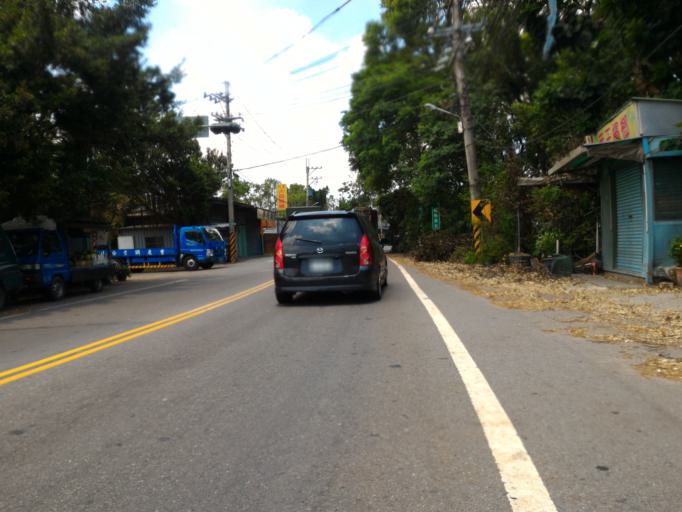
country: TW
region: Taipei
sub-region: Taipei
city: Banqiao
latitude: 24.9608
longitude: 121.4049
